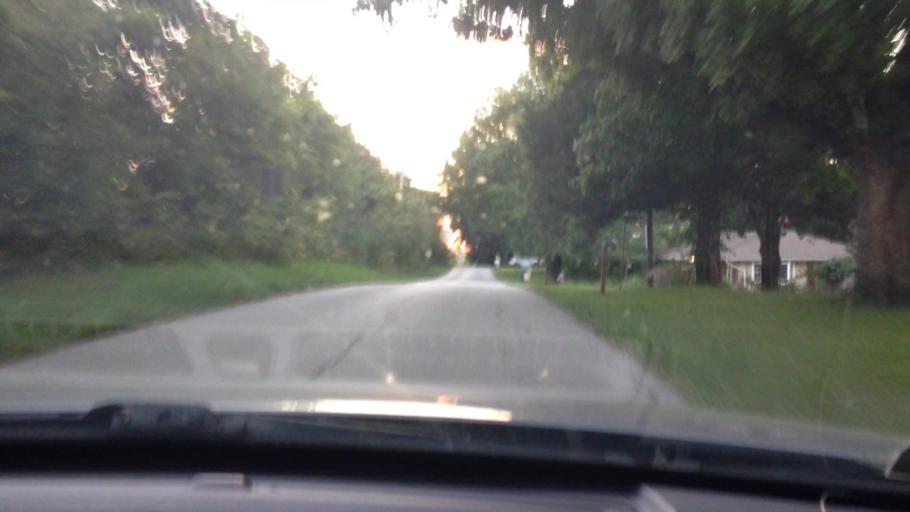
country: US
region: Kansas
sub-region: Leavenworth County
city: Lansing
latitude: 39.1796
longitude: -94.8287
